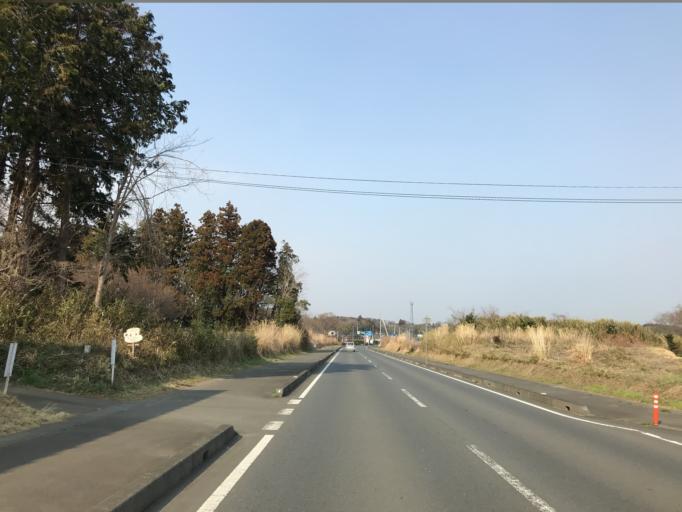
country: JP
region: Ibaraki
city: Okunoya
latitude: 36.2147
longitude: 140.4071
